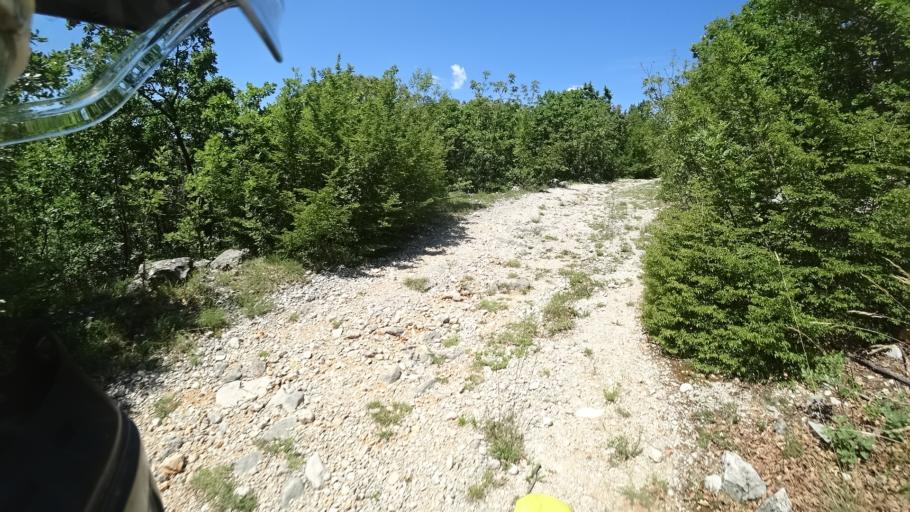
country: HR
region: Sibensko-Kniniska
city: Knin
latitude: 44.0119
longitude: 16.3360
